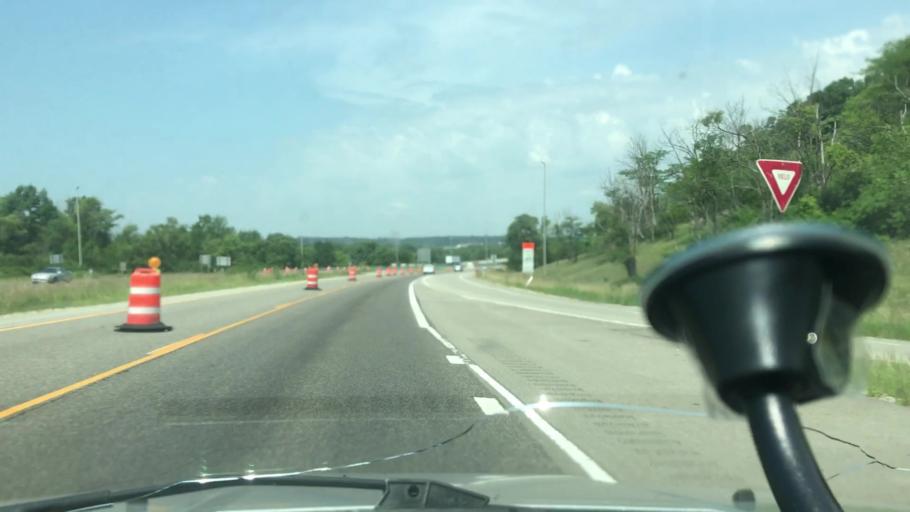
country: US
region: Illinois
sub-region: Tazewell County
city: North Pekin
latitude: 40.6305
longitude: -89.6149
